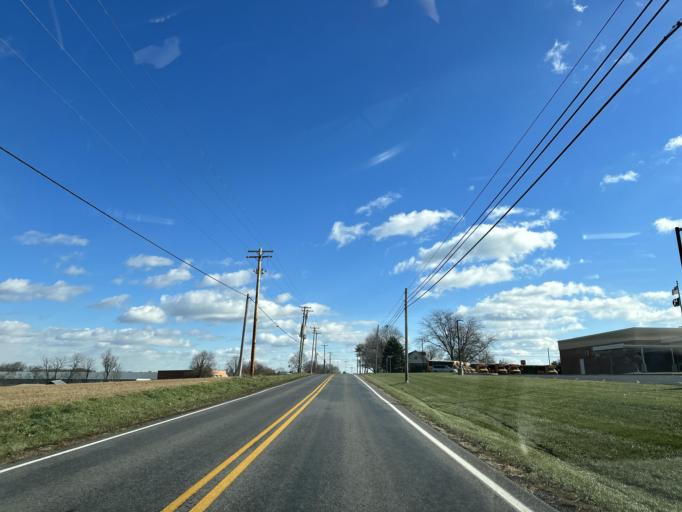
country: US
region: Pennsylvania
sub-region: Lebanon County
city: Myerstown
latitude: 40.4598
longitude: -76.2637
